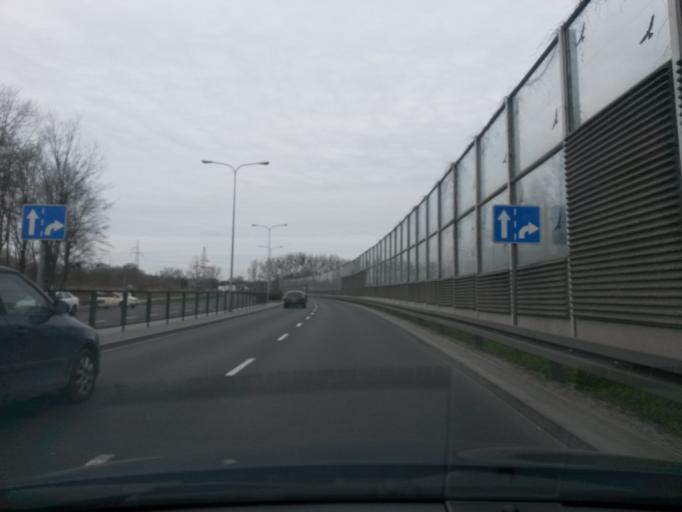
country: PL
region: Greater Poland Voivodeship
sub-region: Poznan
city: Poznan
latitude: 52.4386
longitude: 16.9524
